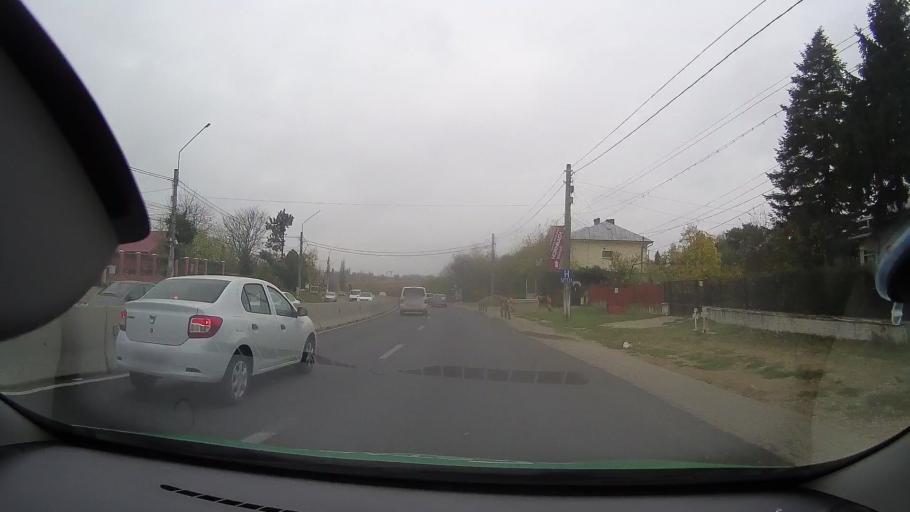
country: RO
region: Ilfov
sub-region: Comuna Corbeanca
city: Corbeanca
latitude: 44.6167
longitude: 26.0695
